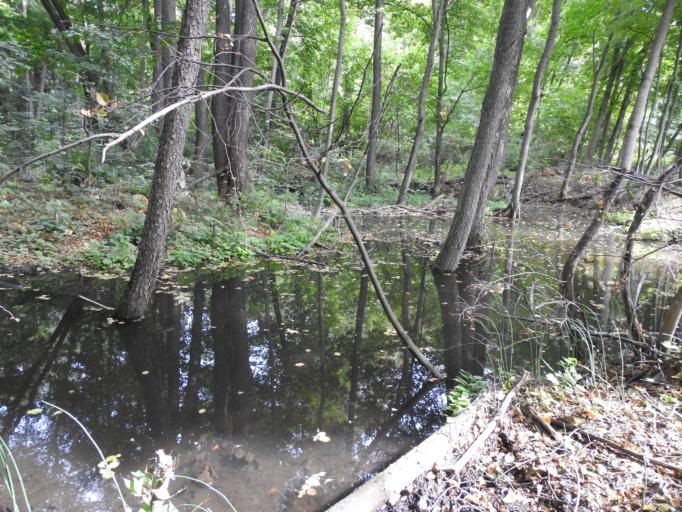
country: RU
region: Saratov
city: Novyye Burasy
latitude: 52.1467
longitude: 46.2165
